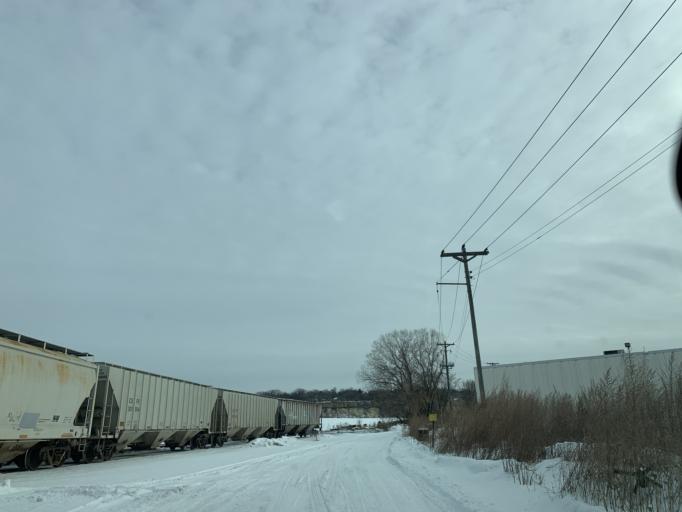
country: US
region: Minnesota
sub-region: Ramsey County
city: Saint Paul
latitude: 44.9457
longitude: -93.0755
